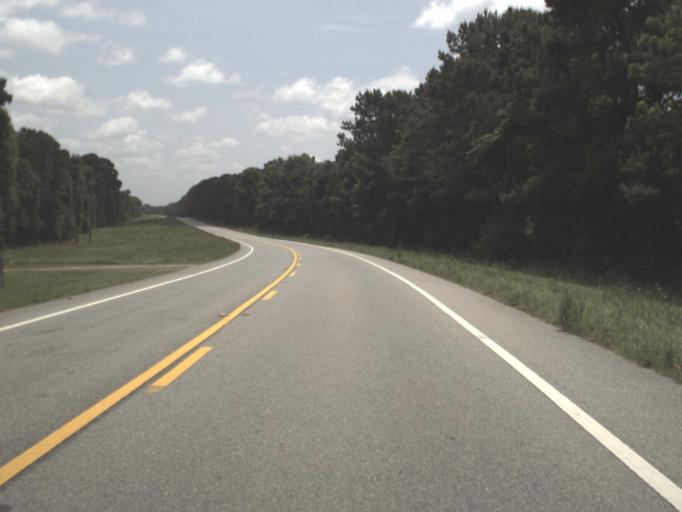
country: US
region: Florida
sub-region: Madison County
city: Madison
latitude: 30.4685
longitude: -83.5833
